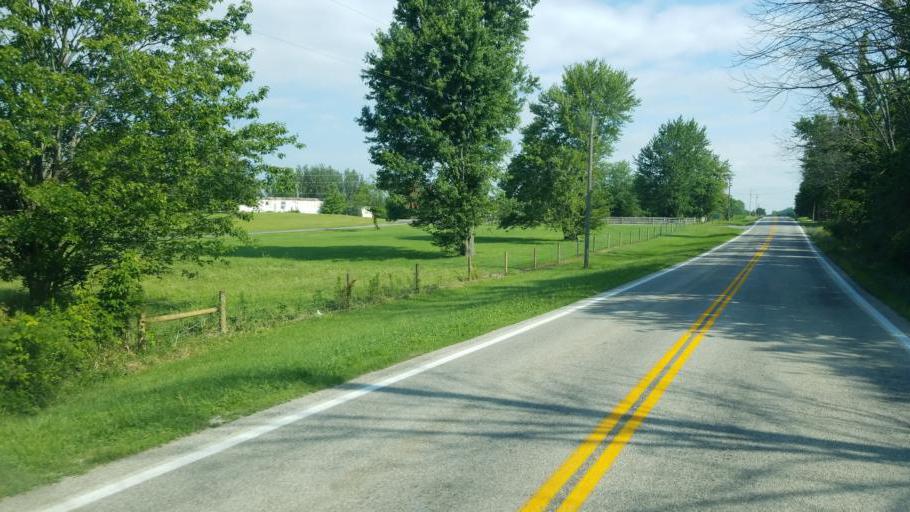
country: US
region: Ohio
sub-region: Crawford County
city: Galion
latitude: 40.6335
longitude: -82.7657
